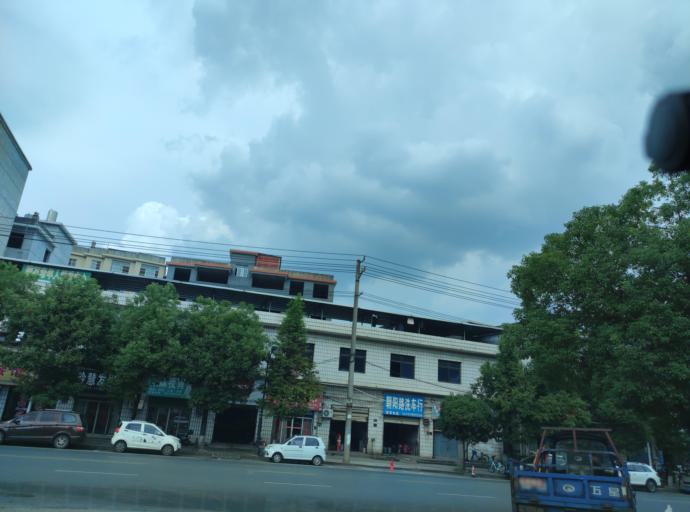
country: CN
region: Jiangxi Sheng
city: Pingxiang
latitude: 27.6601
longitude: 113.8389
